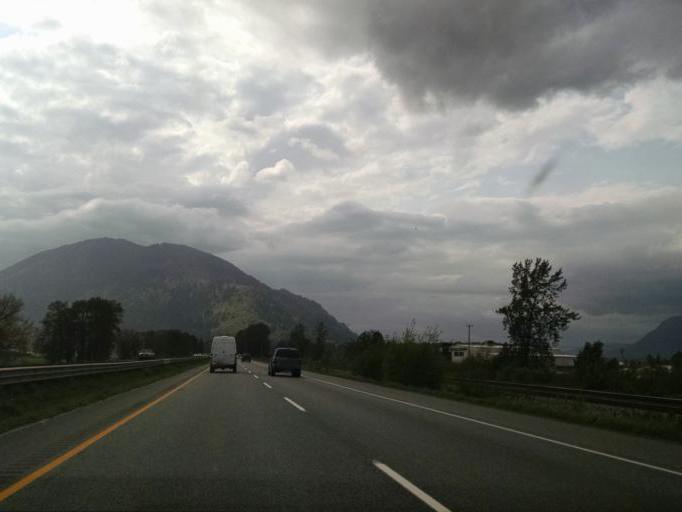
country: CA
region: British Columbia
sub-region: Fraser Valley Regional District
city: Chilliwack
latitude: 49.1391
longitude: -122.0542
